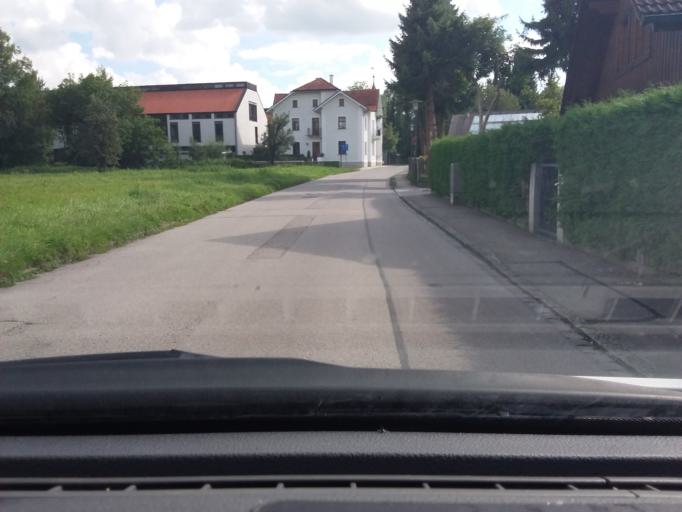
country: DE
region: Bavaria
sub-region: Upper Bavaria
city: Ismaning
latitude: 48.2233
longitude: 11.6762
